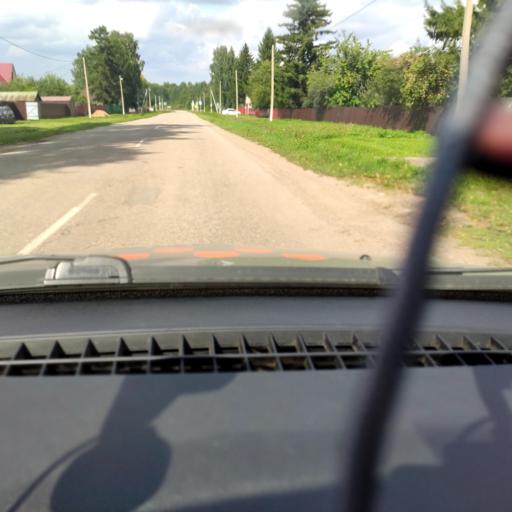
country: RU
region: Bashkortostan
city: Kudeyevskiy
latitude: 54.7271
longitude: 56.6107
